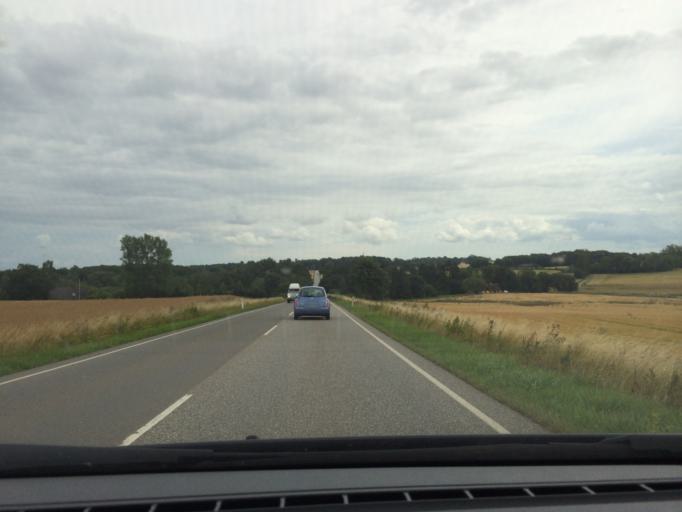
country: DK
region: Zealand
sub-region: Vordingborg Kommune
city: Praesto
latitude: 55.1039
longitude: 12.0711
